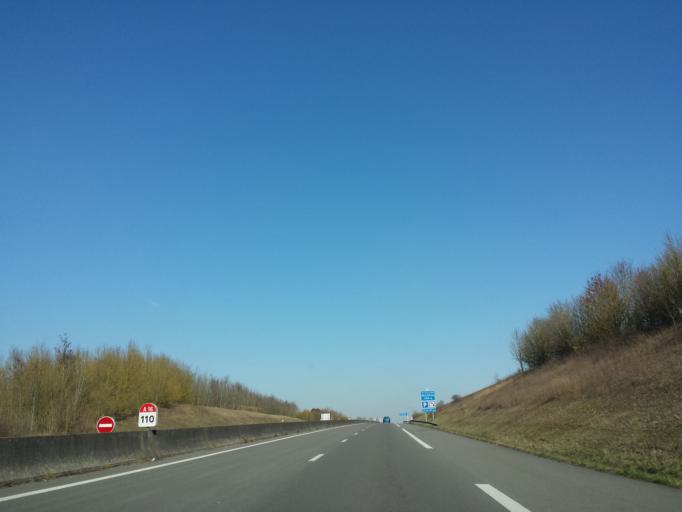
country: FR
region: Picardie
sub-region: Departement de la Somme
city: Conty
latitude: 49.7535
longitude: 2.2302
